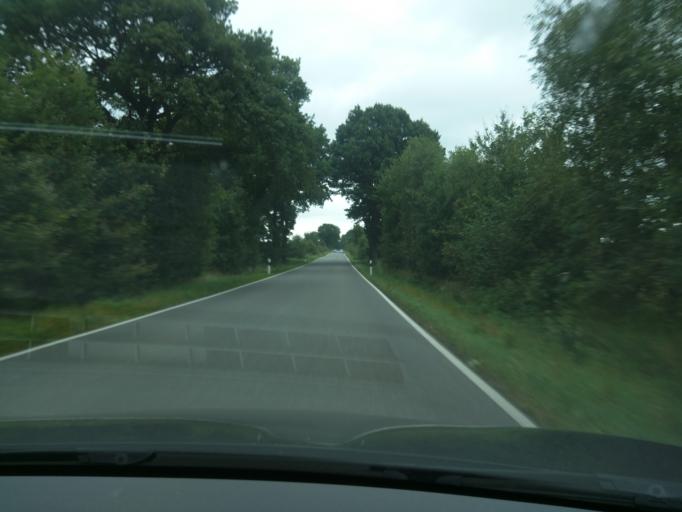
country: DE
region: Schleswig-Holstein
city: Gottin
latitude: 53.5248
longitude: 10.7102
